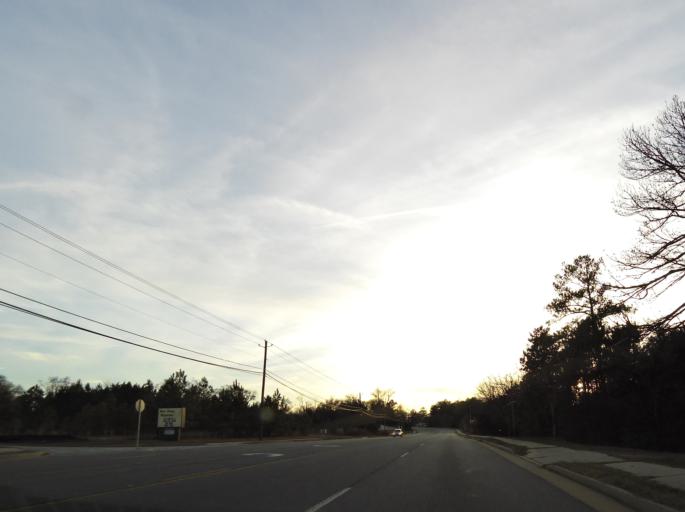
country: US
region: Georgia
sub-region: Bibb County
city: Macon
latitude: 32.7539
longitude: -83.6663
